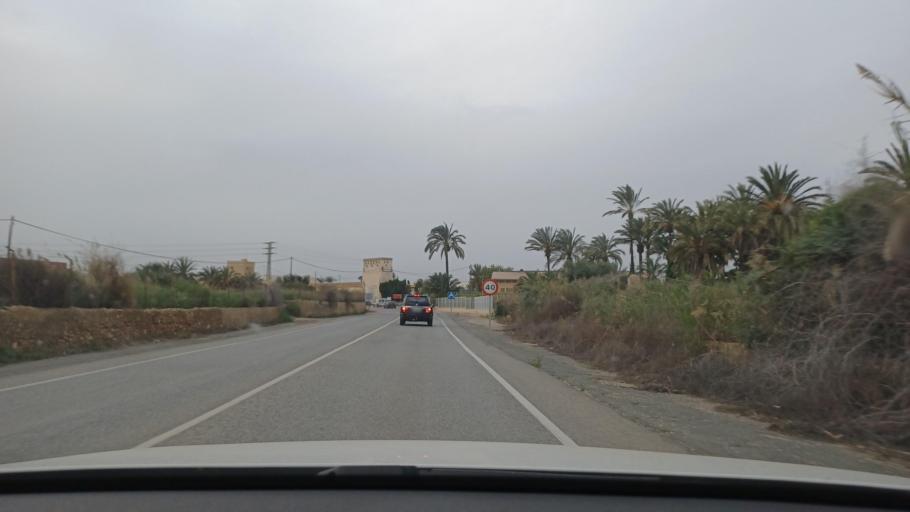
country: ES
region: Valencia
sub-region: Provincia de Alicante
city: Elche
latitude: 38.2487
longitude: -0.6900
